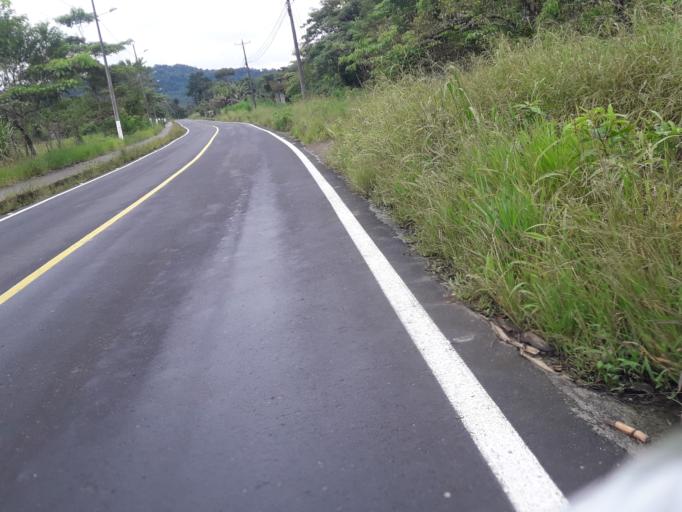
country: EC
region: Napo
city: Tena
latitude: -0.9711
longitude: -77.8555
